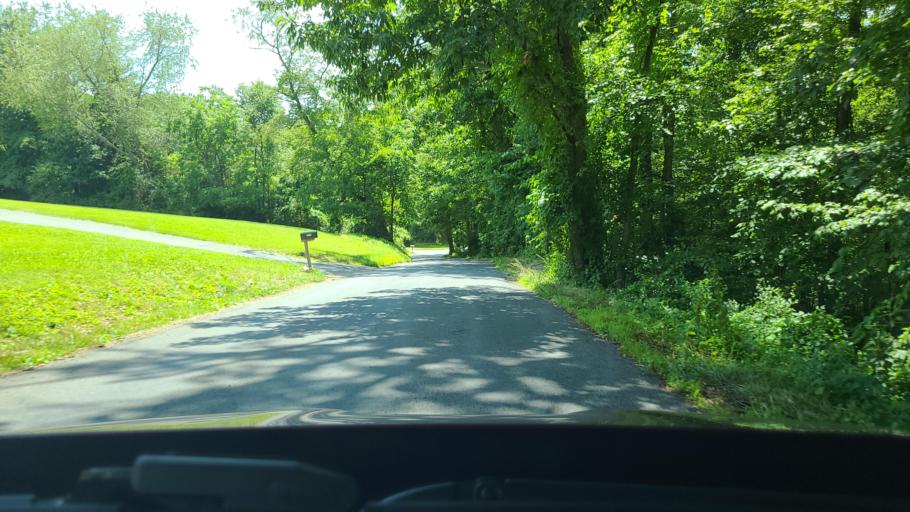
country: US
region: Maryland
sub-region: Montgomery County
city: Damascus
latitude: 39.2689
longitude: -77.2329
